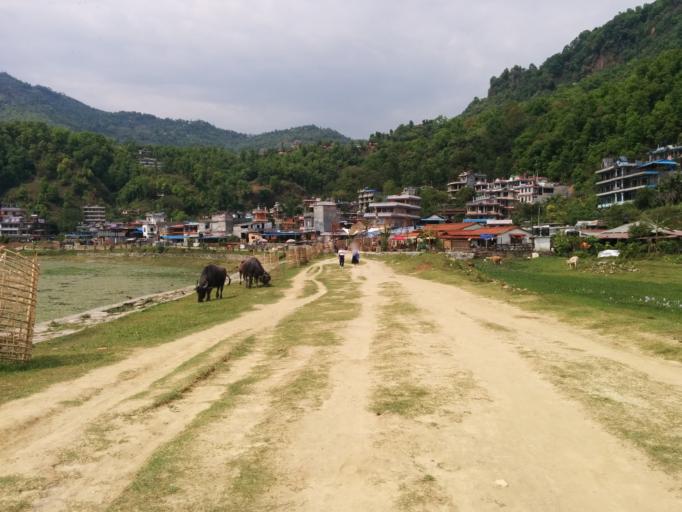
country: NP
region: Western Region
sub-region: Gandaki Zone
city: Pokhara
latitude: 28.2184
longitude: 83.9576
